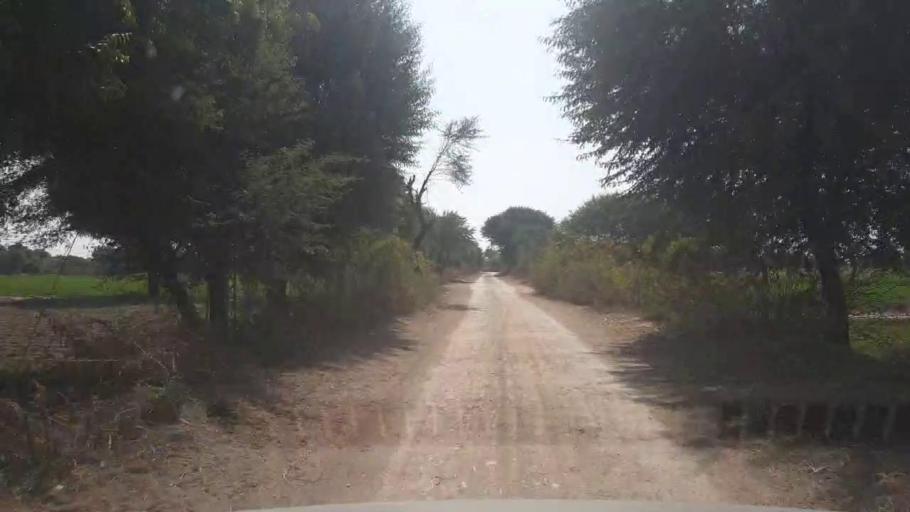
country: PK
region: Sindh
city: Chambar
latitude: 25.2697
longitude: 68.8118
